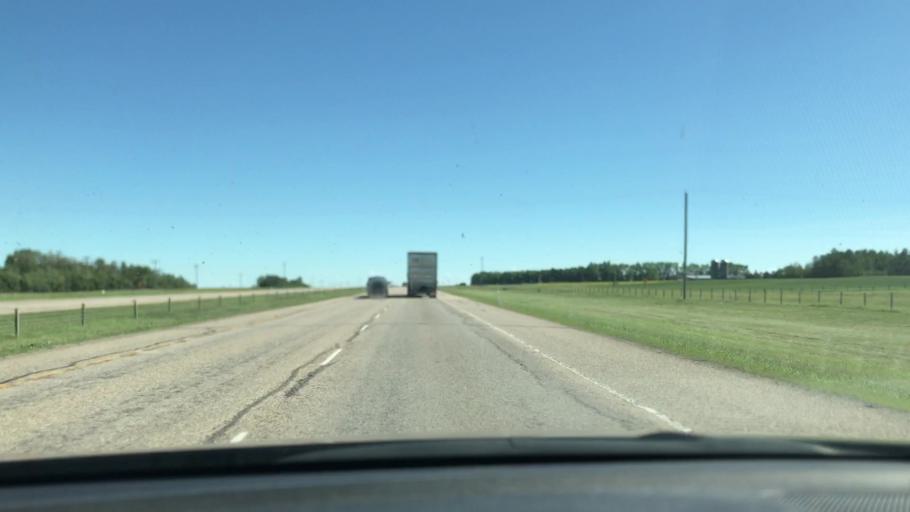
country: CA
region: Alberta
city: Olds
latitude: 51.8858
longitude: -114.0256
